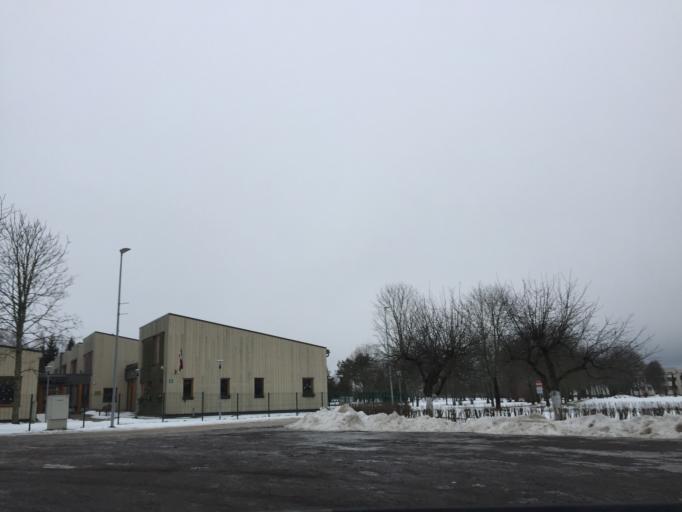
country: LV
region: Krimulda
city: Ragana
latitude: 57.1803
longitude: 24.7005
